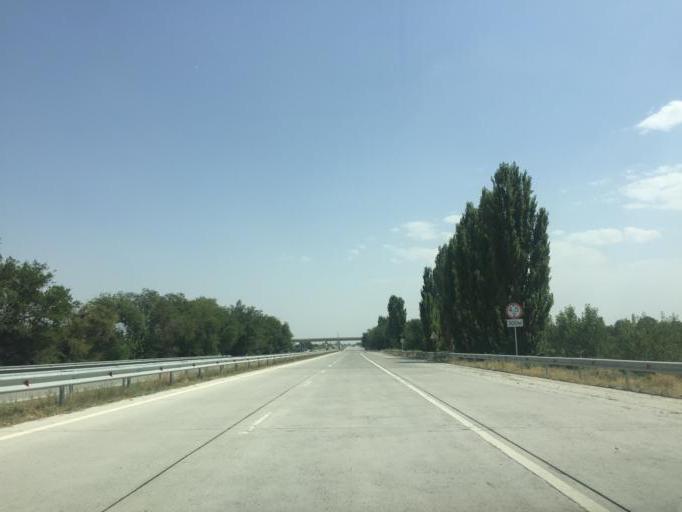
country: AM
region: Ararat
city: Burastan
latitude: 39.9768
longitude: 44.4970
